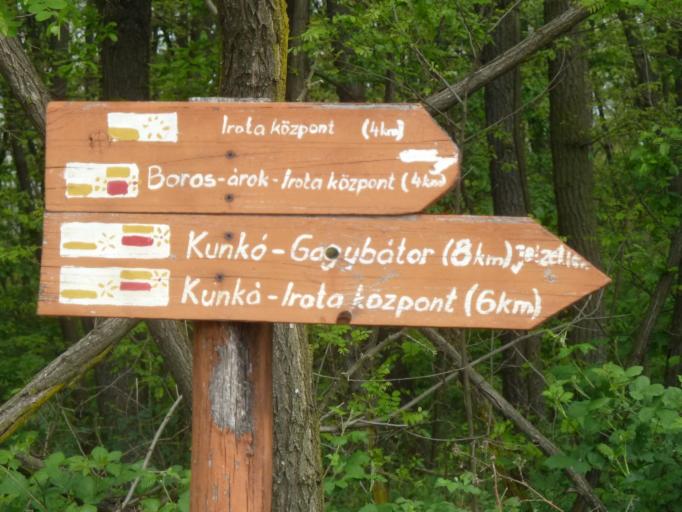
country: HU
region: Borsod-Abauj-Zemplen
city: Szendro
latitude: 48.4260
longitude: 20.8784
